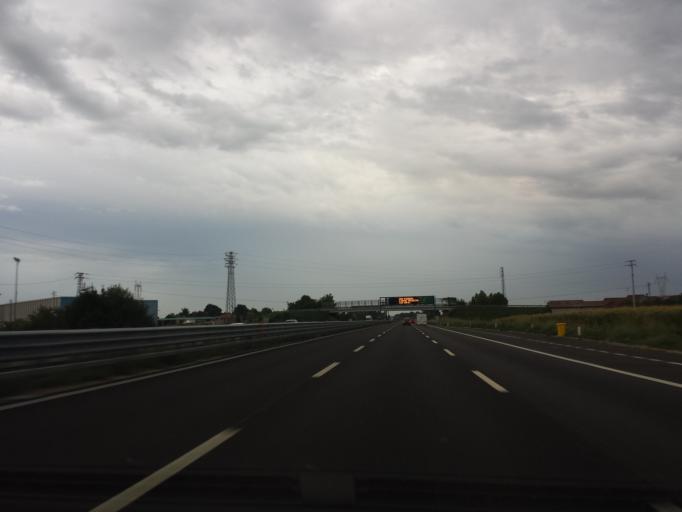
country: IT
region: Veneto
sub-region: Provincia di Vicenza
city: Grumolo delle Abbadesse
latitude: 45.4968
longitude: 11.6494
